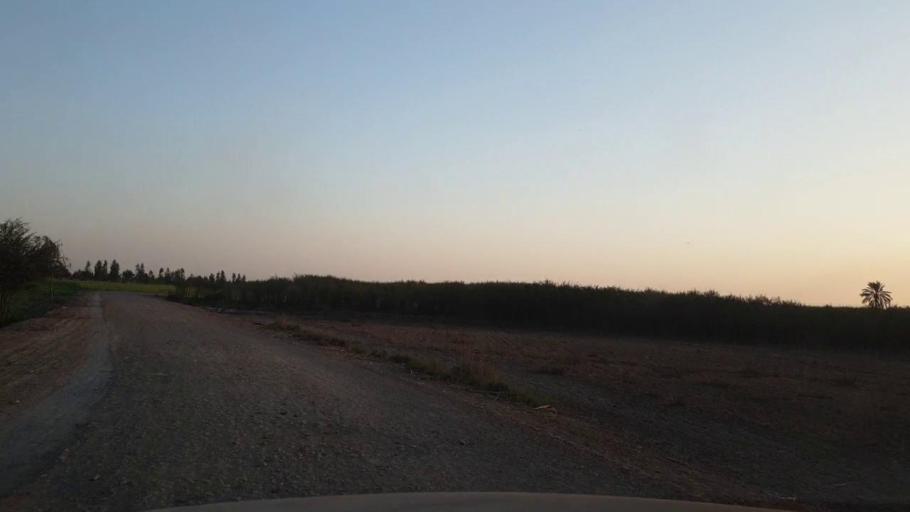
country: PK
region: Sindh
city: Tando Allahyar
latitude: 25.5551
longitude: 68.6416
